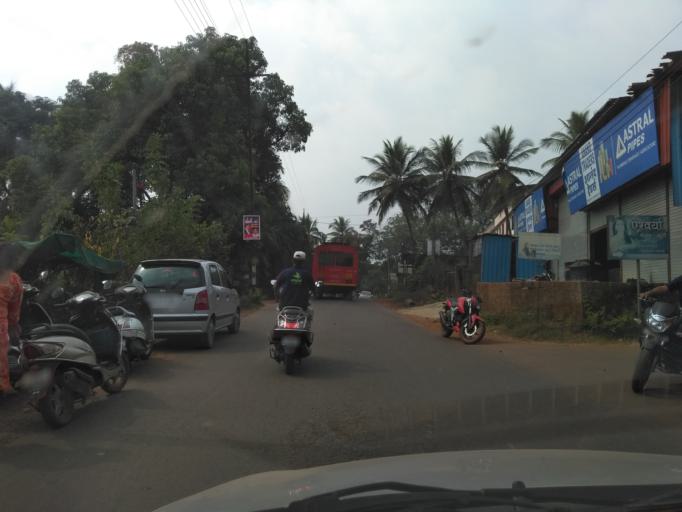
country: IN
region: Maharashtra
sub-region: Sindhudurg
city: Kudal
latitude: 16.0079
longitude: 73.6852
